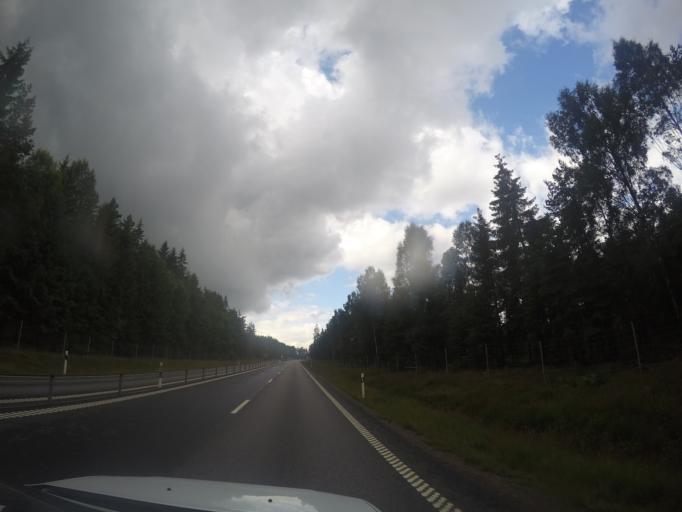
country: SE
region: Kronoberg
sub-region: Ljungby Kommun
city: Ljungby
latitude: 56.8063
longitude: 13.8832
